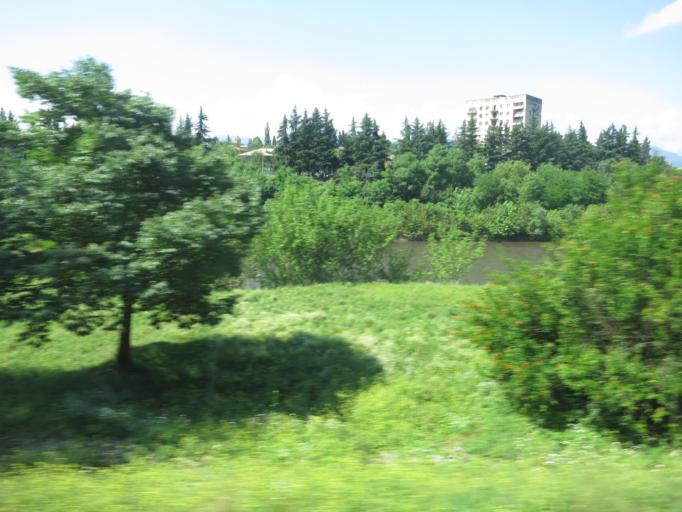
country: GE
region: Imereti
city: Zestap'oni
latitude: 42.1081
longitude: 43.0522
